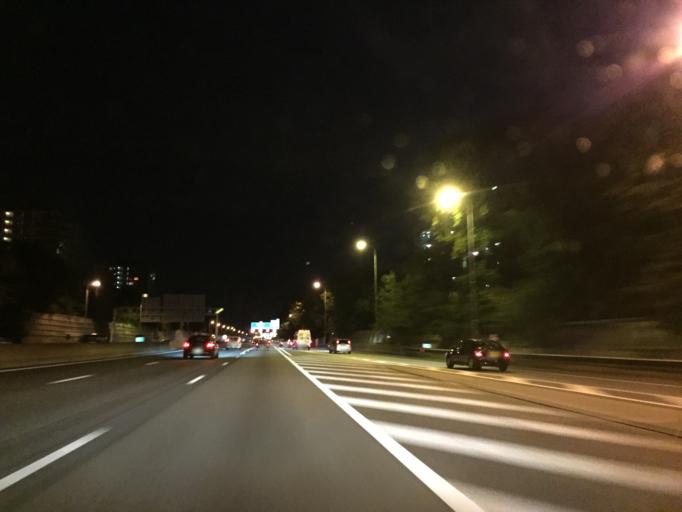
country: NL
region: North Holland
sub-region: Gemeente Amsterdam
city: Amsterdam
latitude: 52.3688
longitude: 4.8420
